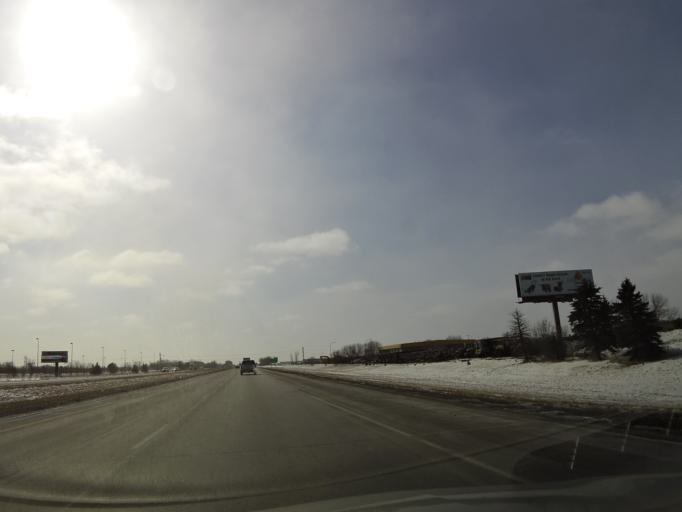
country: US
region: North Dakota
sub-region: Grand Forks County
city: Grand Forks
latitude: 47.9120
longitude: -97.0938
